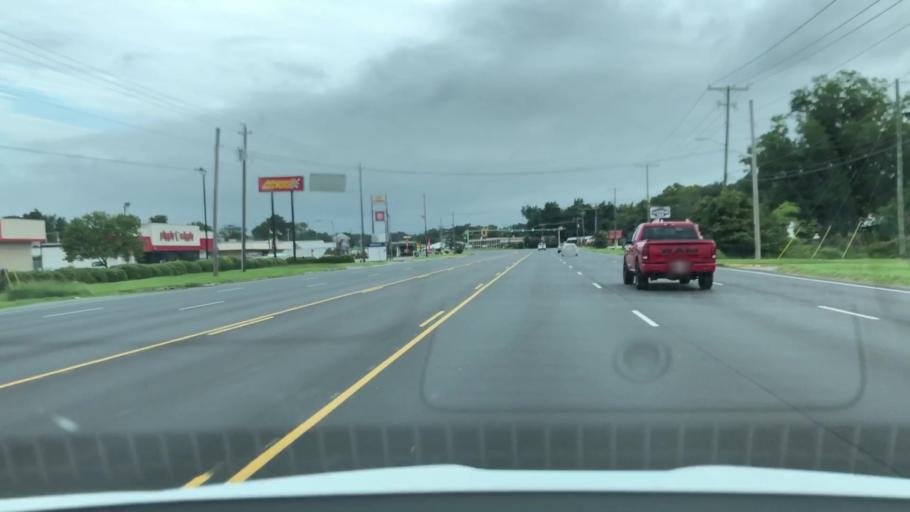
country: US
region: North Carolina
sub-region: Lenoir County
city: Kinston
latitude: 35.2404
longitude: -77.5770
